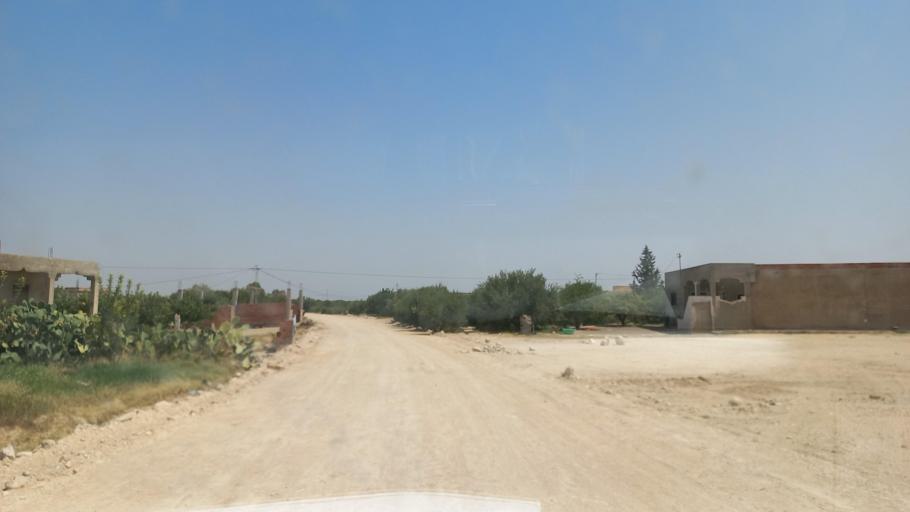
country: TN
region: Al Qasrayn
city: Kasserine
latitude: 35.2472
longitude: 9.0252
